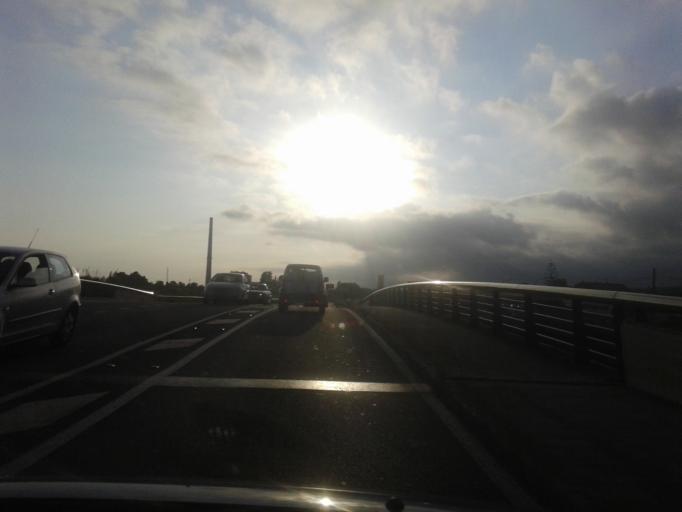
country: ES
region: Catalonia
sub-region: Provincia de Barcelona
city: Cubelles
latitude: 41.2067
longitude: 1.6700
